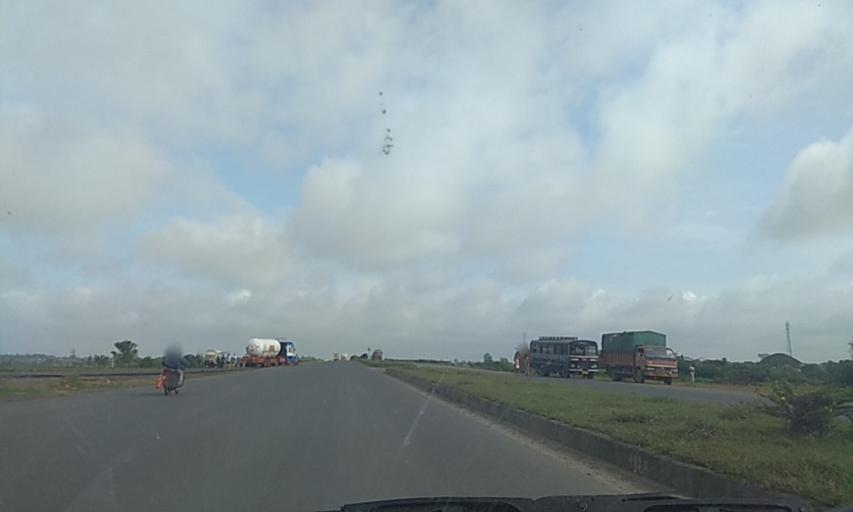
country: IN
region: Karnataka
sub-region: Haveri
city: Haveri
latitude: 14.8610
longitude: 75.3227
